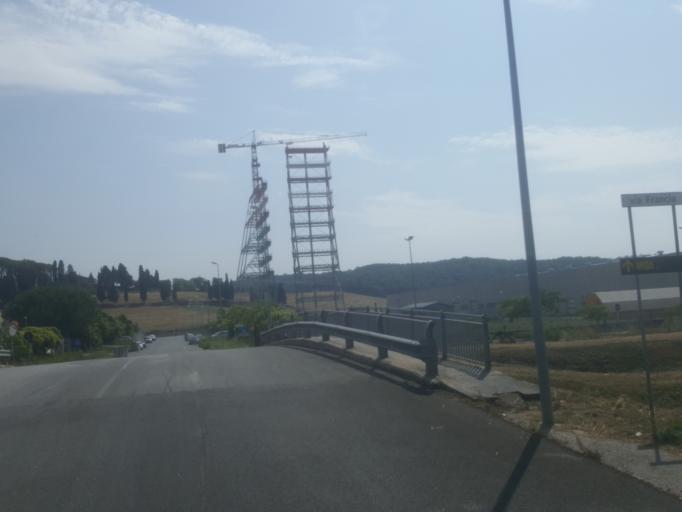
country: IT
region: Tuscany
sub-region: Provincia di Livorno
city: Guasticce
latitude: 43.5955
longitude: 10.4004
